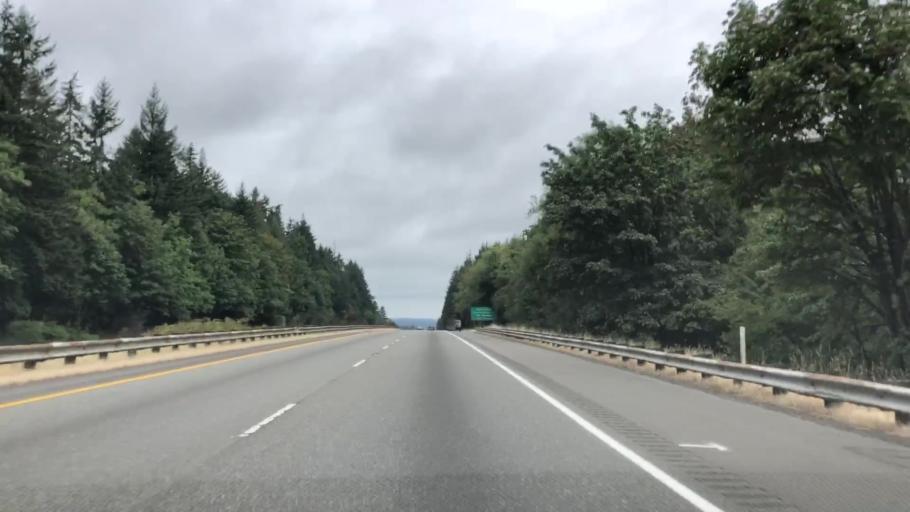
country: US
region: Washington
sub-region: Pierce County
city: Gig Harbor
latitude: 47.3471
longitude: -122.6094
